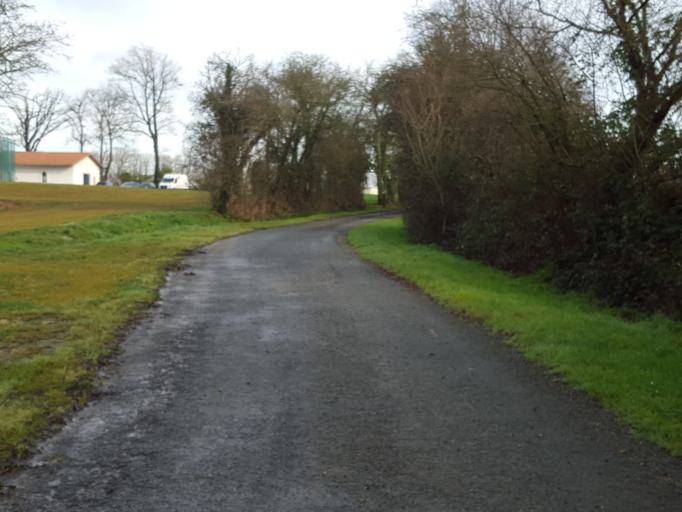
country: FR
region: Pays de la Loire
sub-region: Departement de la Vendee
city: Mouilleron-le-Captif
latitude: 46.7110
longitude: -1.4370
